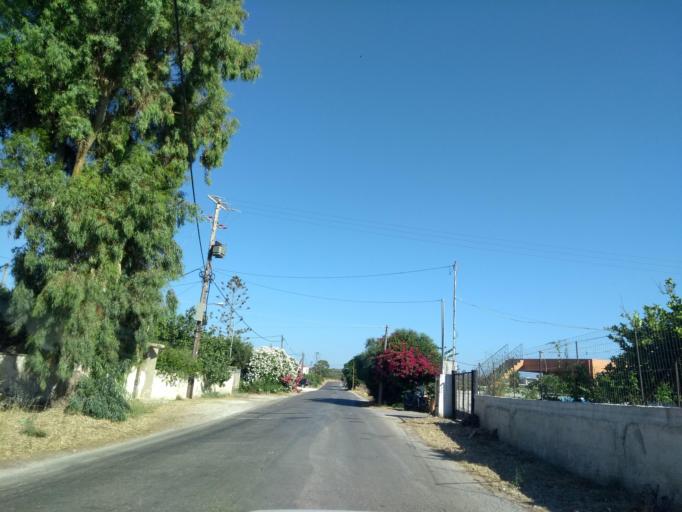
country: GR
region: Crete
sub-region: Nomos Chanias
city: Pithari
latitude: 35.5840
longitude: 24.0900
